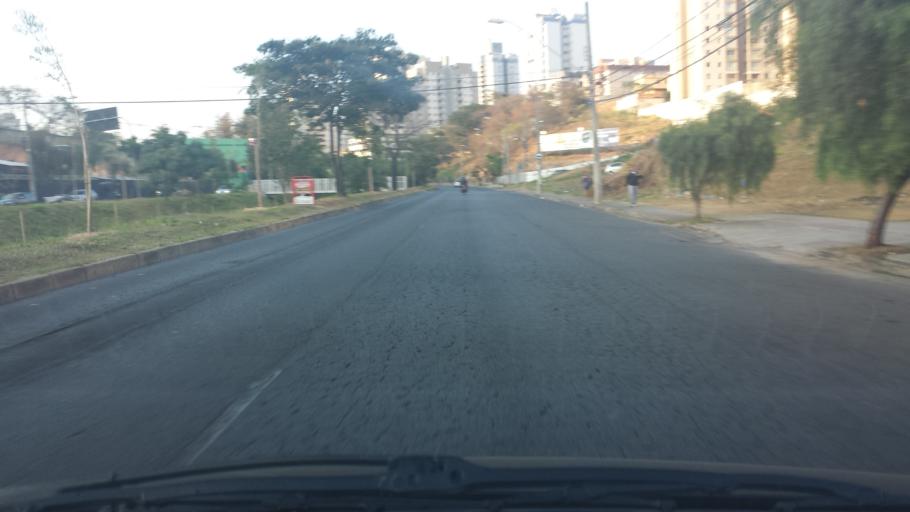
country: BR
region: Minas Gerais
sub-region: Belo Horizonte
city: Belo Horizonte
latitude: -19.8848
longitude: -43.9938
